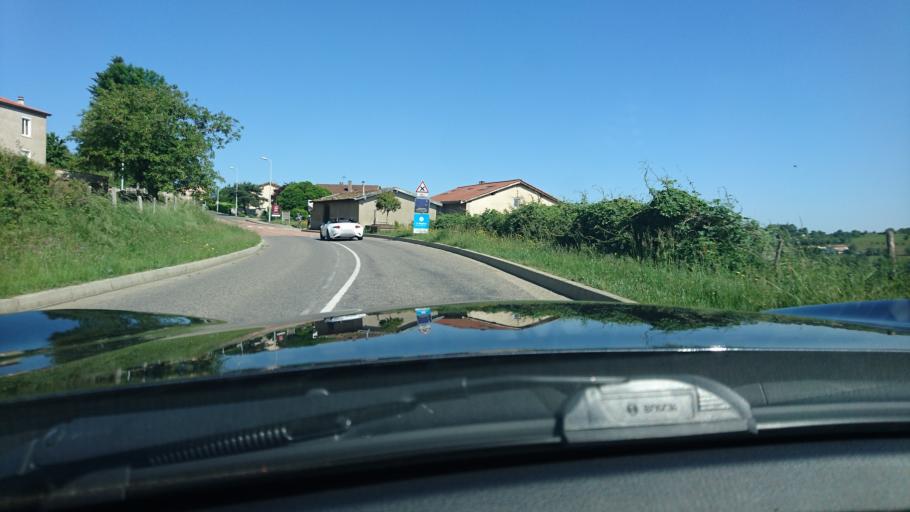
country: FR
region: Rhone-Alpes
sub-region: Departement du Rhone
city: Bessenay
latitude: 45.7772
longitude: 4.5580
